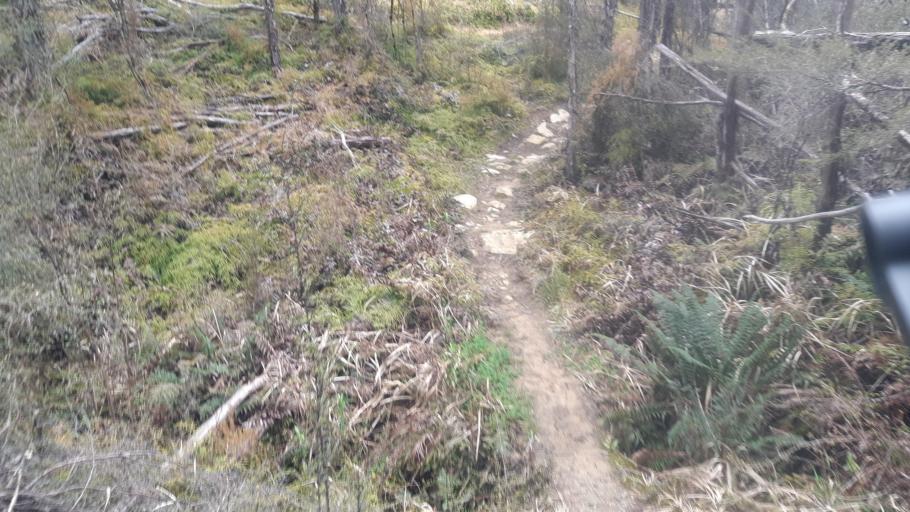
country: NZ
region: Tasman
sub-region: Tasman District
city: Wakefield
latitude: -41.7769
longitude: 172.8096
